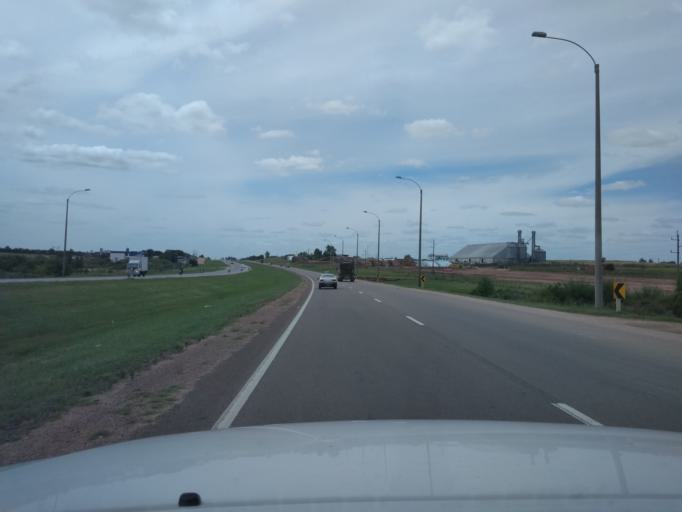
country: UY
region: Canelones
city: La Paz
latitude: -34.7485
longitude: -56.2540
